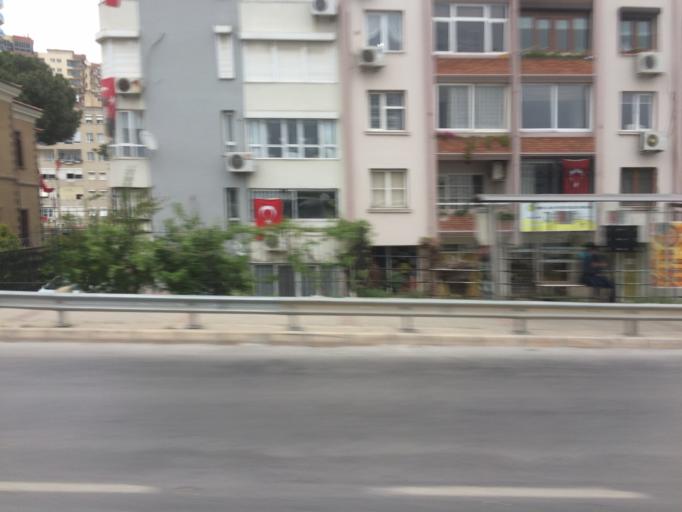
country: TR
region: Izmir
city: Karsiyaka
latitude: 38.4666
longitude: 27.1604
